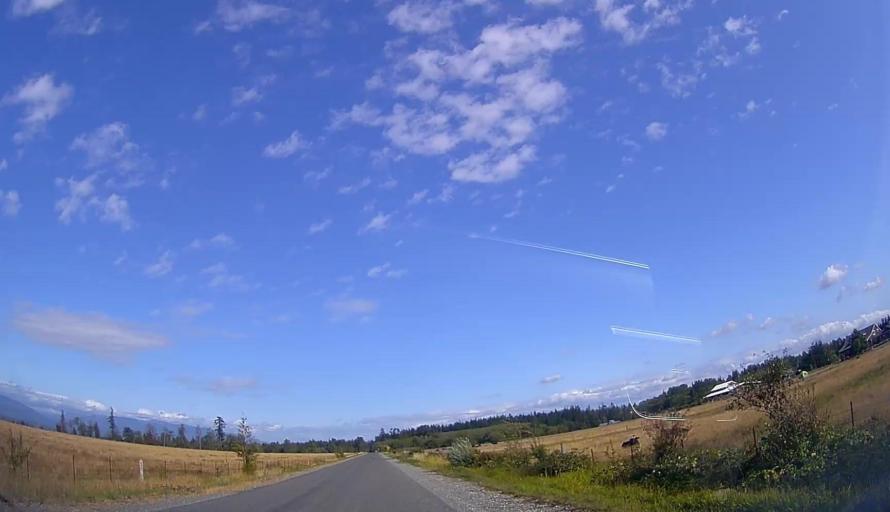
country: US
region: Washington
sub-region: Skagit County
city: Burlington
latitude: 48.5012
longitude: -122.4659
